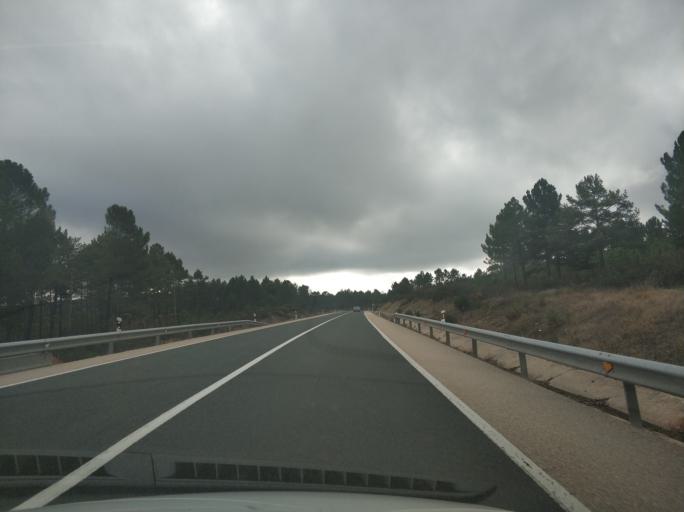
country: ES
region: Castille and Leon
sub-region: Provincia de Soria
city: Muriel Viejo
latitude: 41.8220
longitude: -2.9402
